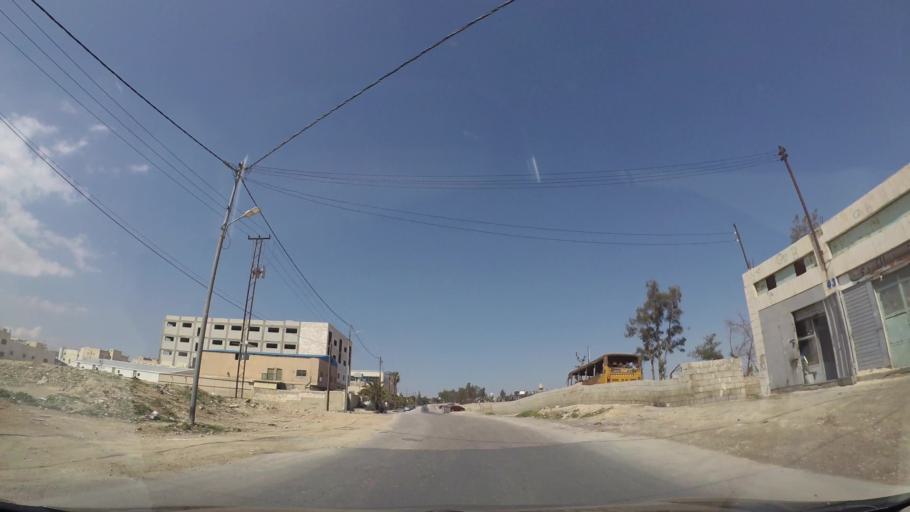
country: JO
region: Zarqa
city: Russeifa
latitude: 31.9934
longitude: 36.0122
